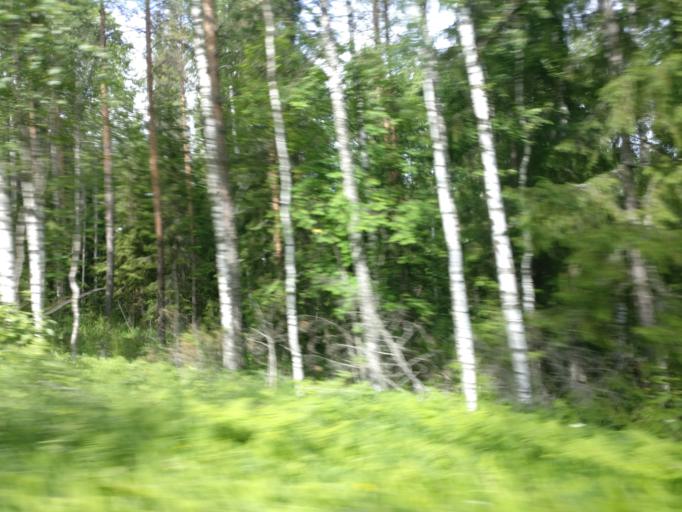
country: FI
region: Southern Savonia
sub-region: Savonlinna
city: Savonlinna
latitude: 61.9847
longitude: 28.8023
